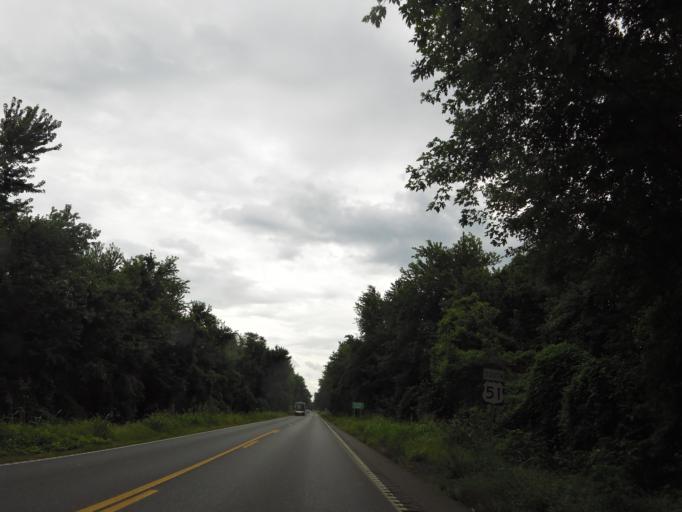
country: US
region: Illinois
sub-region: Alexander County
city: Cairo
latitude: 36.9998
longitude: -89.1346
